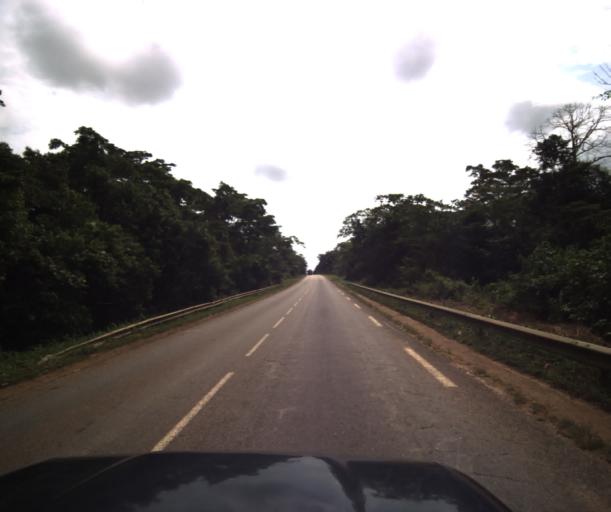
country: CM
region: Centre
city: Eseka
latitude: 3.8497
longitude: 10.5061
